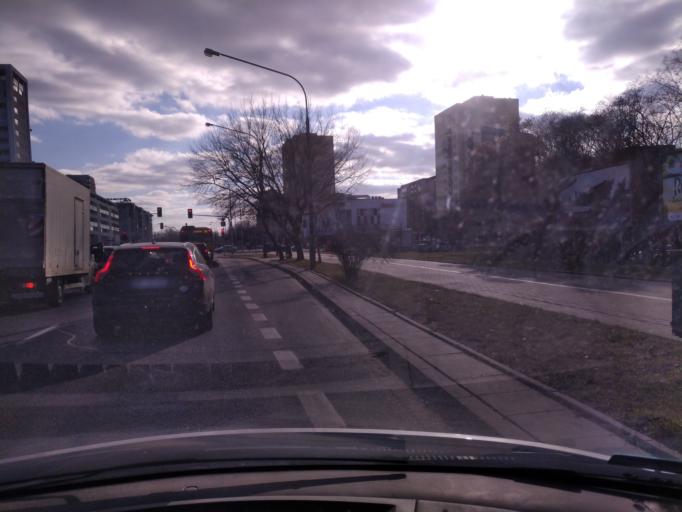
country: PL
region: Masovian Voivodeship
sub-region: Warszawa
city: Praga Poludnie
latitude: 52.2259
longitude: 21.0928
